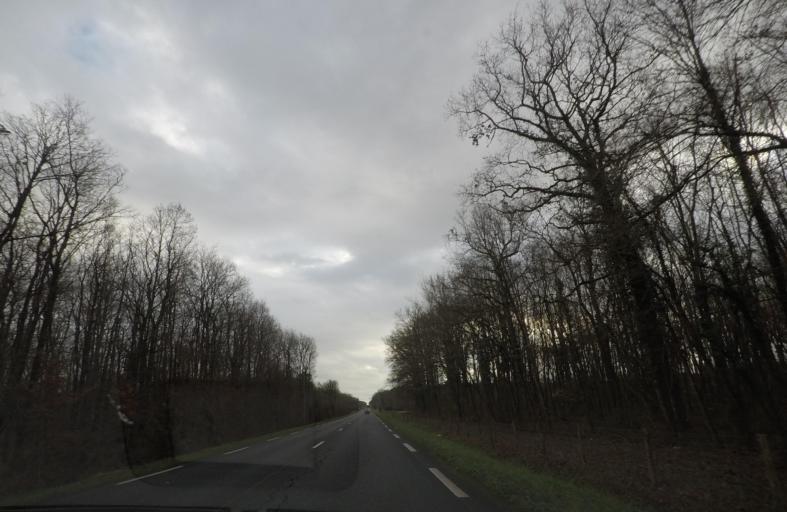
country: FR
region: Centre
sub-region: Departement du Loir-et-Cher
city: Mur-de-Sologne
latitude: 47.4296
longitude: 1.5683
